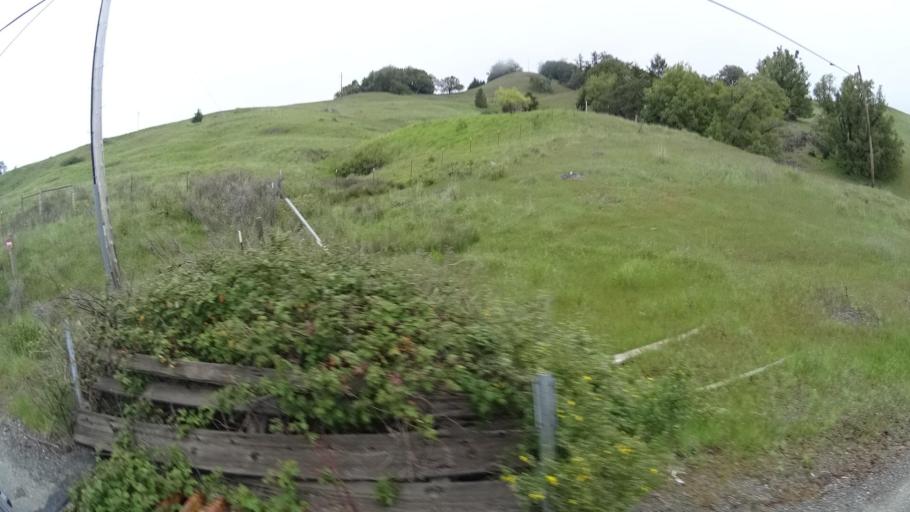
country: US
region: California
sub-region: Humboldt County
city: Redway
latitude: 40.1099
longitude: -123.7171
